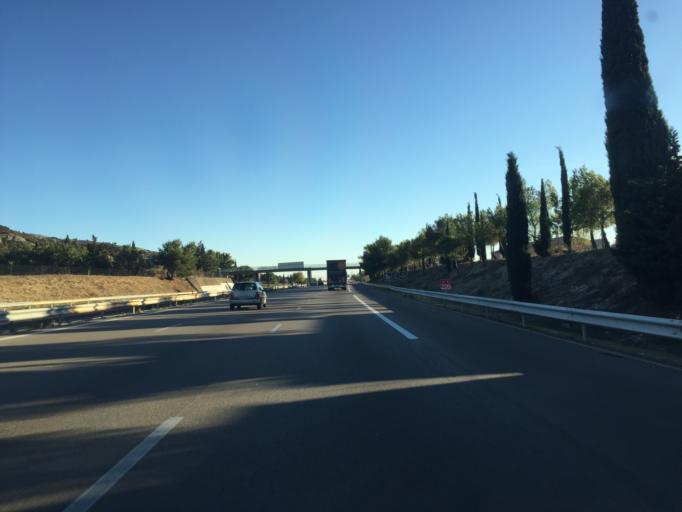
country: FR
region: Provence-Alpes-Cote d'Azur
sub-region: Departement des Bouches-du-Rhone
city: Lamanon
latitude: 43.6993
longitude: 5.0984
